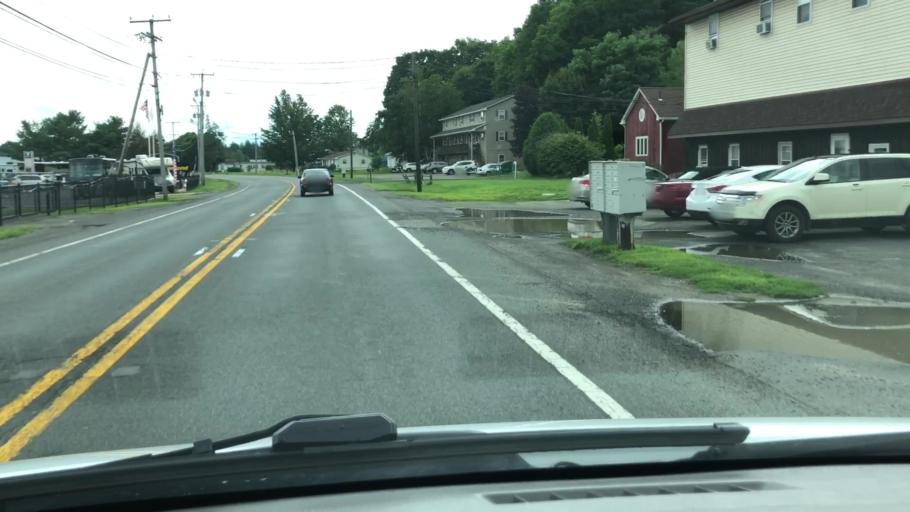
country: US
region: Massachusetts
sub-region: Hampshire County
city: Hatfield
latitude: 42.3916
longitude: -72.6330
